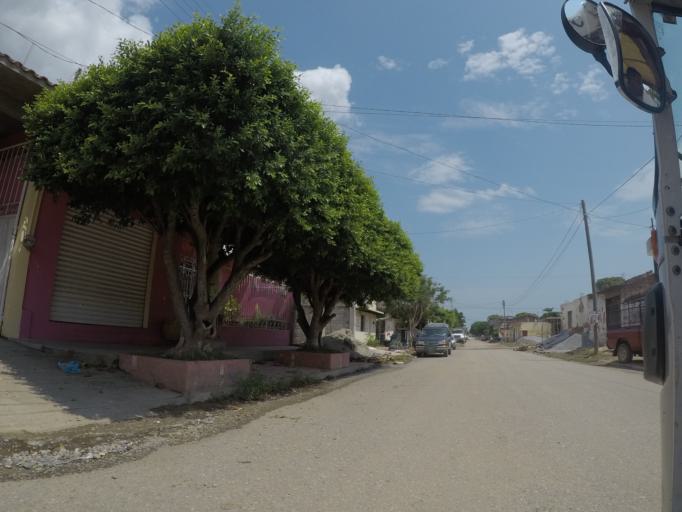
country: MX
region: Oaxaca
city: Union Hidalgo
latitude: 16.4721
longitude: -94.8282
